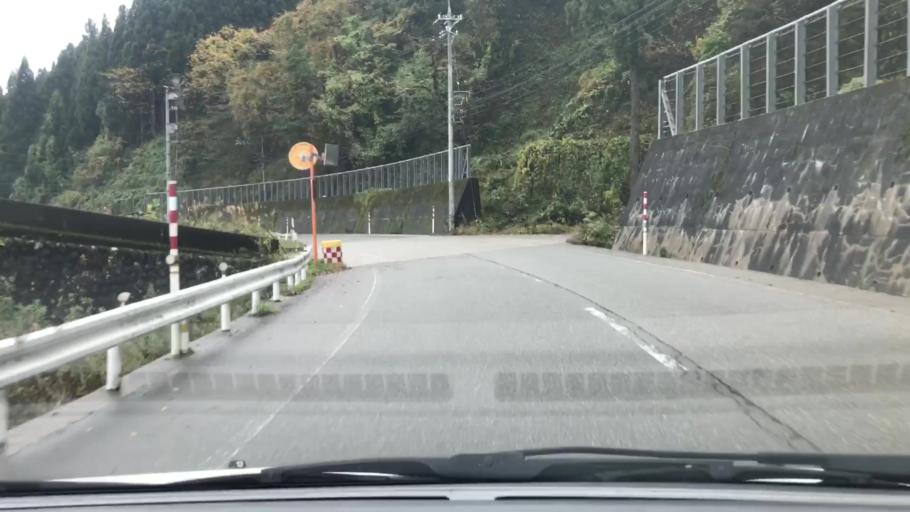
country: JP
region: Toyama
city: Kamiichi
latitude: 36.5775
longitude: 137.3319
